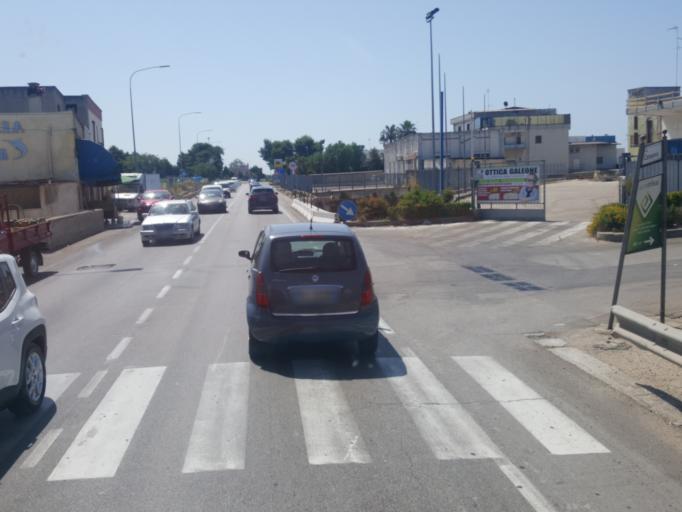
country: IT
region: Apulia
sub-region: Provincia di Taranto
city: Massafra
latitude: 40.5847
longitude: 17.1094
